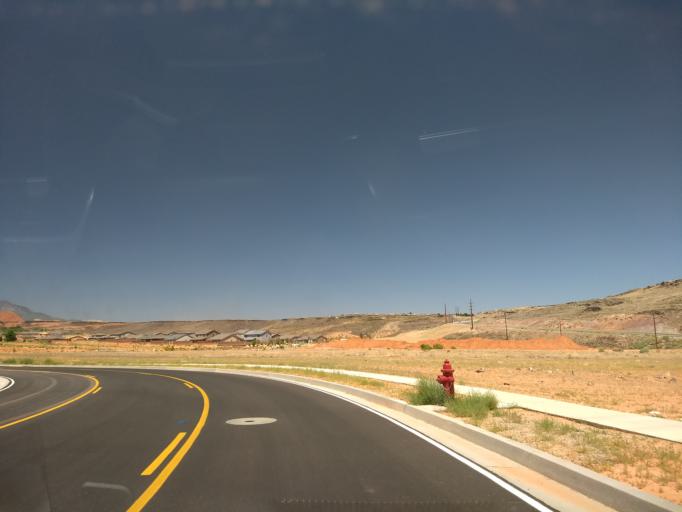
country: US
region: Utah
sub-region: Washington County
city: Washington
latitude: 37.1333
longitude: -113.4836
